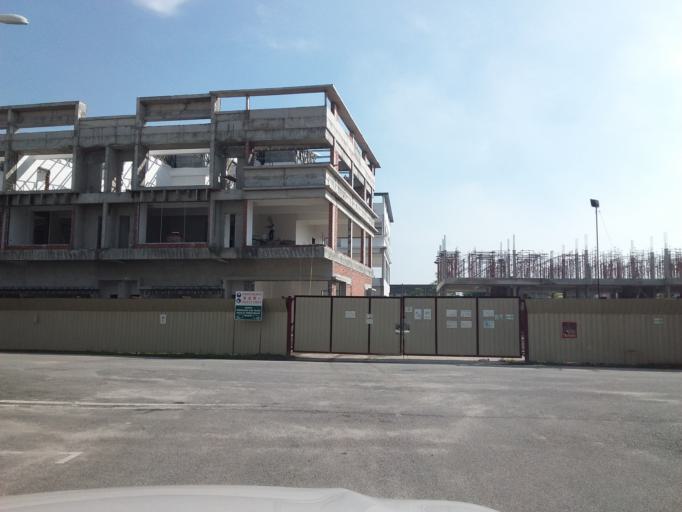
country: MY
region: Johor
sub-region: Daerah Batu Pahat
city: Batu Pahat
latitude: 1.8583
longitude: 102.9291
